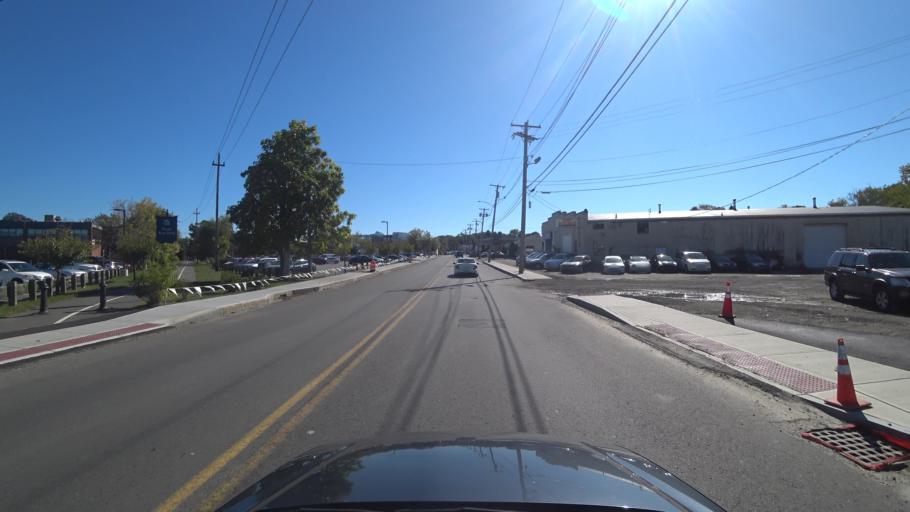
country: US
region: Massachusetts
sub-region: Essex County
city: Salem
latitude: 42.5030
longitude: -70.8961
